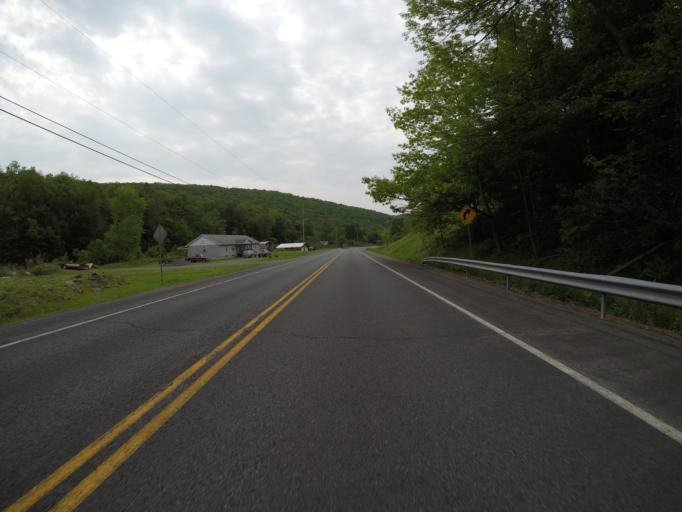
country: US
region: New York
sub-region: Sullivan County
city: Livingston Manor
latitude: 41.9811
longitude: -74.8941
